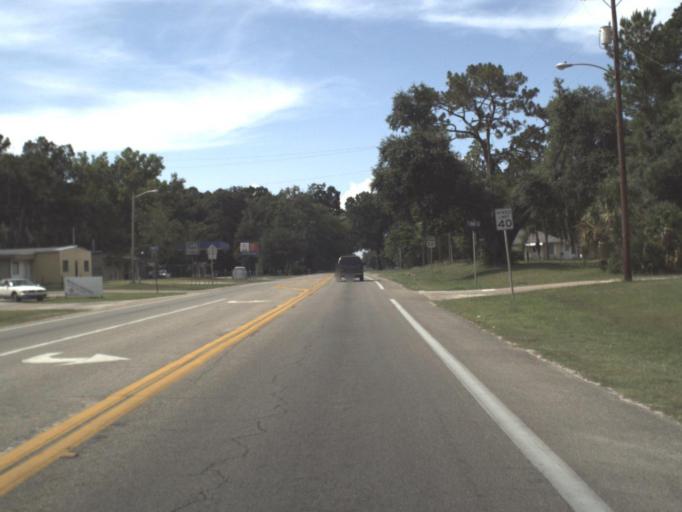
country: US
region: Florida
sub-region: Taylor County
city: Perry
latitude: 30.1286
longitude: -83.5827
